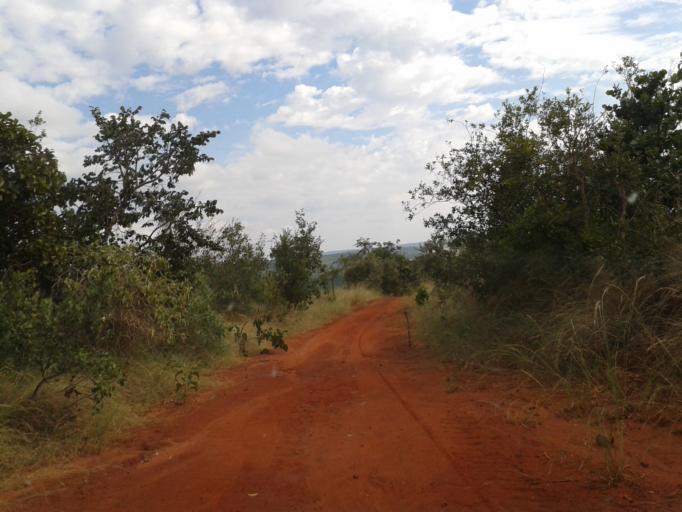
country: BR
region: Minas Gerais
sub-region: Campina Verde
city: Campina Verde
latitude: -19.3929
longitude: -49.6601
